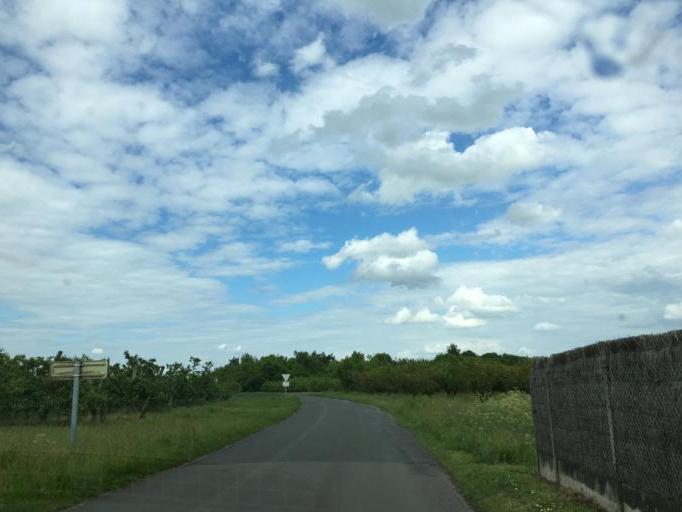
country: FR
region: Centre
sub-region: Departement du Loiret
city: Mareau-aux-Pres
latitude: 47.8345
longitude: 1.8020
